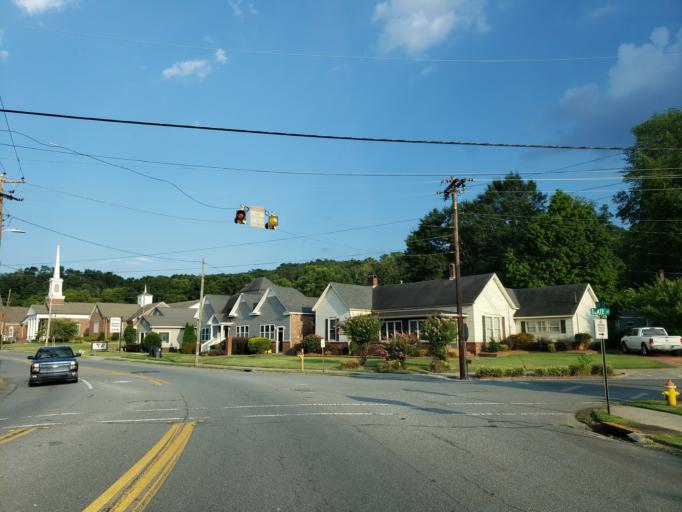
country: US
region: Georgia
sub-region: Polk County
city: Rockmart
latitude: 33.9967
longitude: -85.0503
